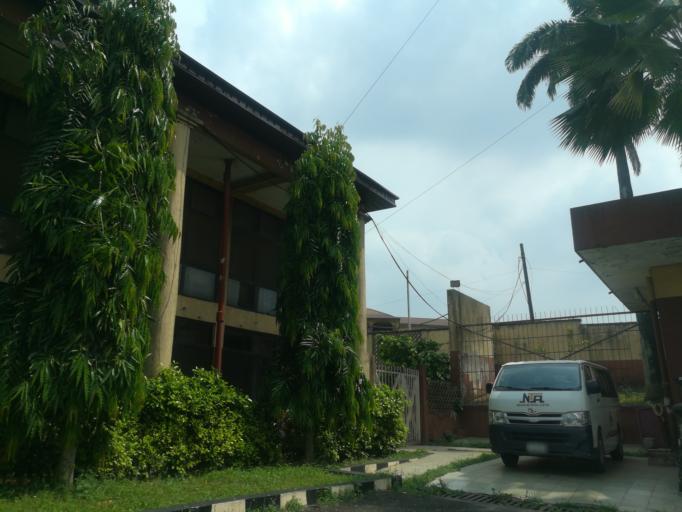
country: NG
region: Oyo
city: Ibadan
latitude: 7.3962
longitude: 3.9169
